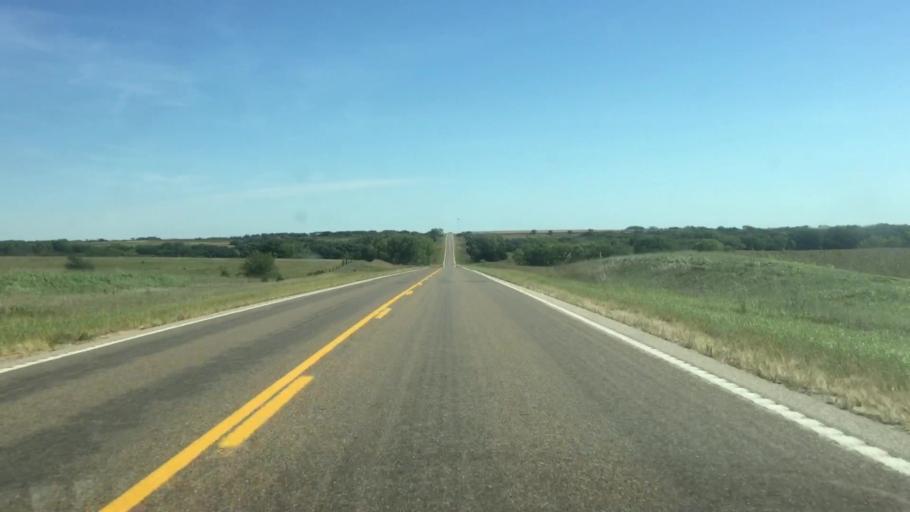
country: US
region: Nebraska
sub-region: Thayer County
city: Hebron
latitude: 40.1472
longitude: -97.5055
